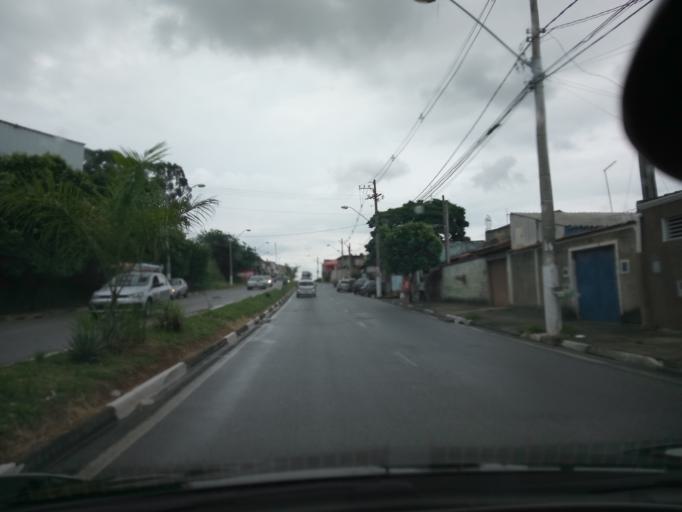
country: BR
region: Sao Paulo
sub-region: Campinas
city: Campinas
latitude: -22.9894
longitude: -47.1152
